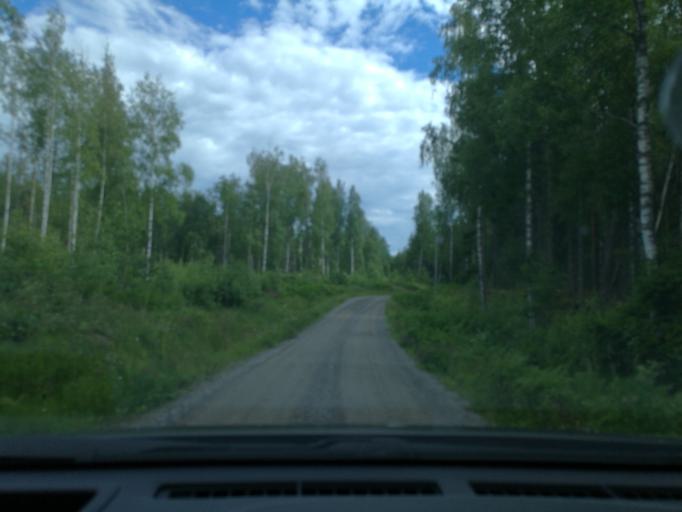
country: SE
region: Vaestmanland
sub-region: Surahammars Kommun
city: Ramnas
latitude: 59.7896
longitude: 16.3076
